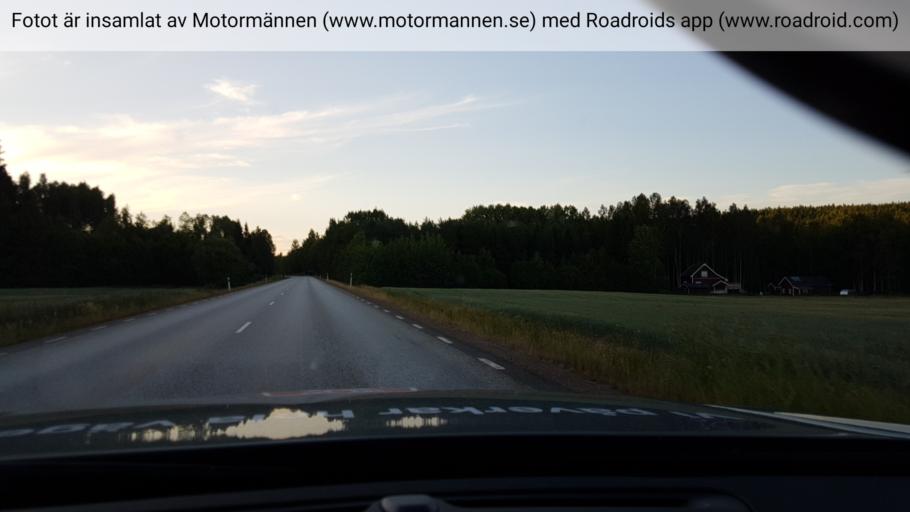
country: SE
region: Vaermland
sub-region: Storfors Kommun
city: Storfors
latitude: 59.5169
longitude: 14.3028
